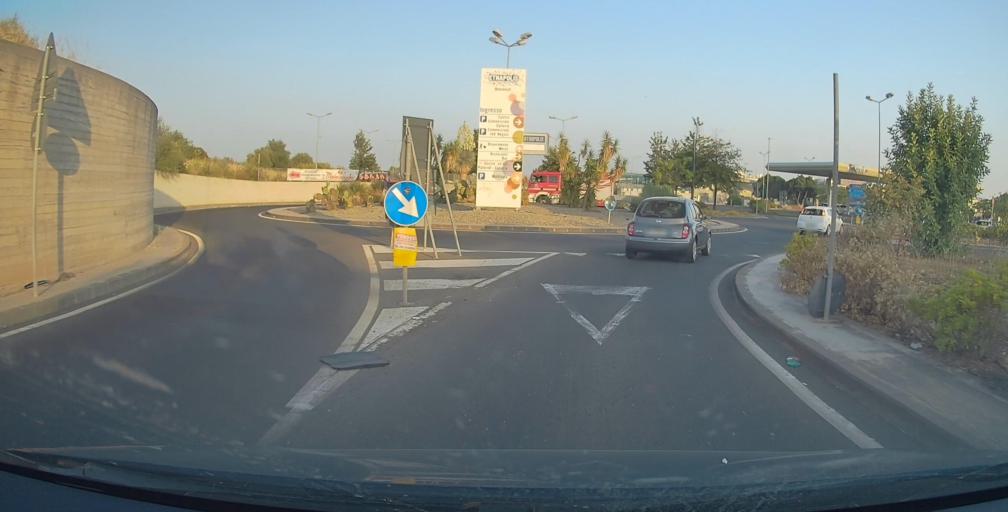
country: IT
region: Sicily
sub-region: Catania
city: Palazzolo
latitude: 37.5489
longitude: 14.9478
